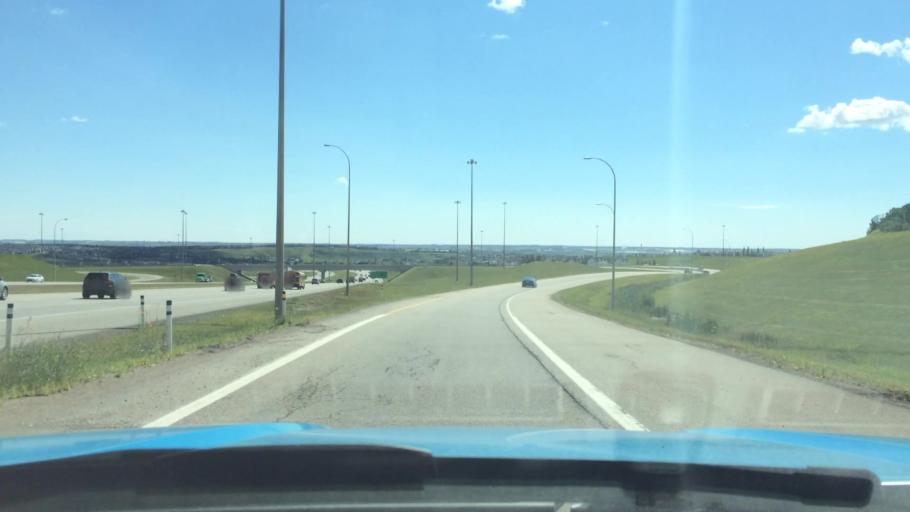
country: CA
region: Alberta
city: Calgary
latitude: 51.1522
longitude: -114.1484
